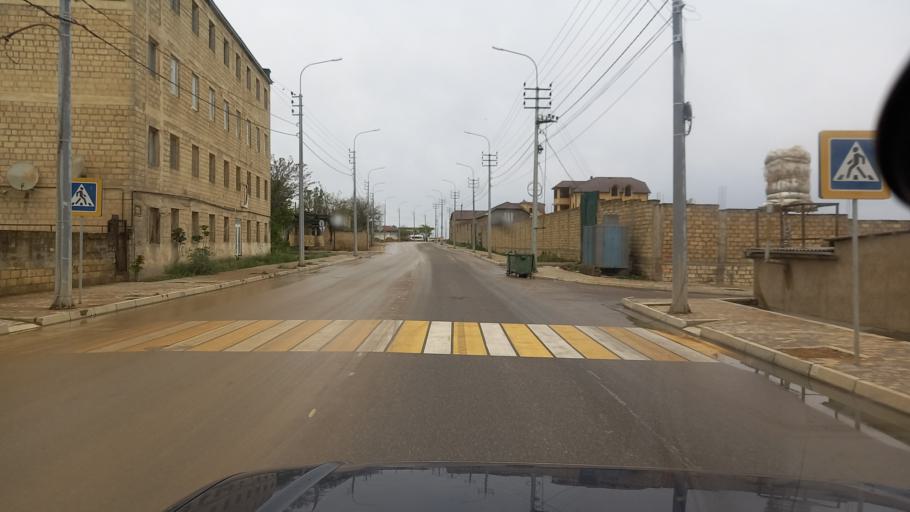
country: RU
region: Dagestan
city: Derbent
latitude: 42.0923
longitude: 48.2885
